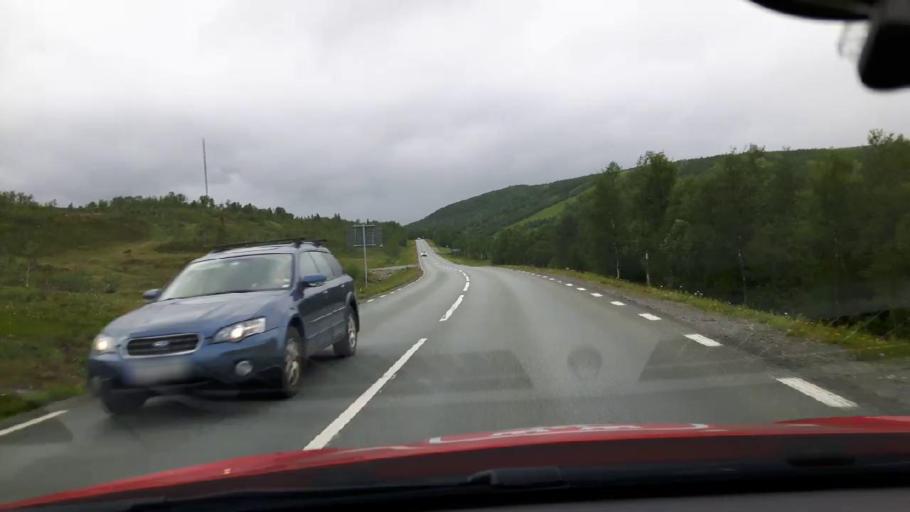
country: NO
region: Nord-Trondelag
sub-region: Meraker
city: Meraker
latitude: 63.3123
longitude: 12.1041
